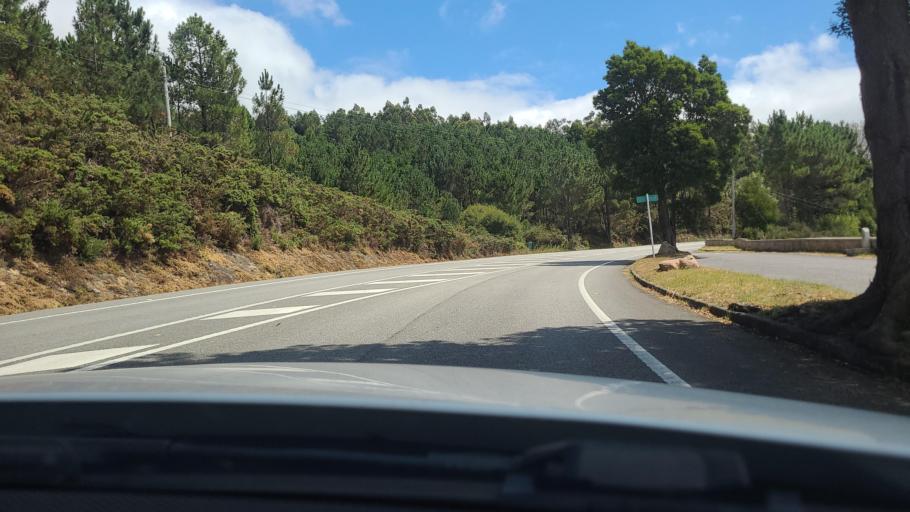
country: ES
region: Galicia
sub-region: Provincia da Coruna
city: Corcubion
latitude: 42.9235
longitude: -9.1568
